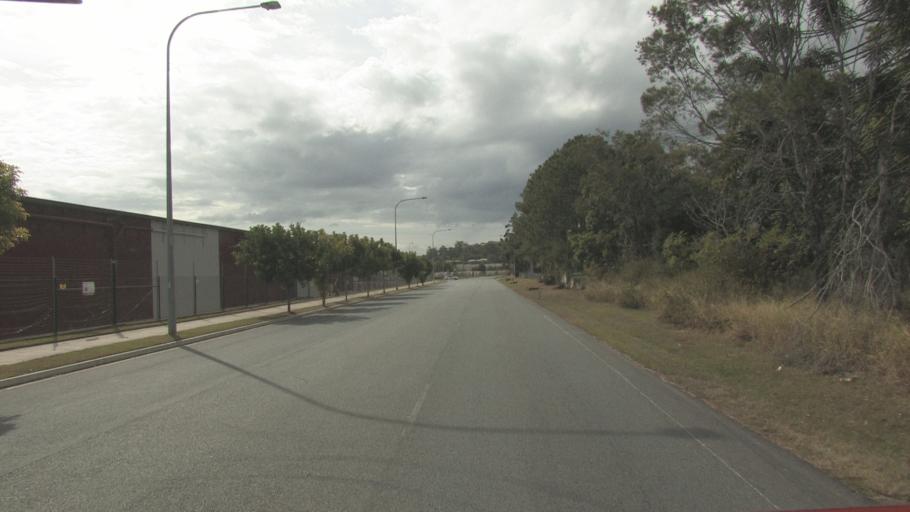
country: AU
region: Queensland
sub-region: Logan
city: Woodridge
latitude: -27.6498
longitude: 153.0945
